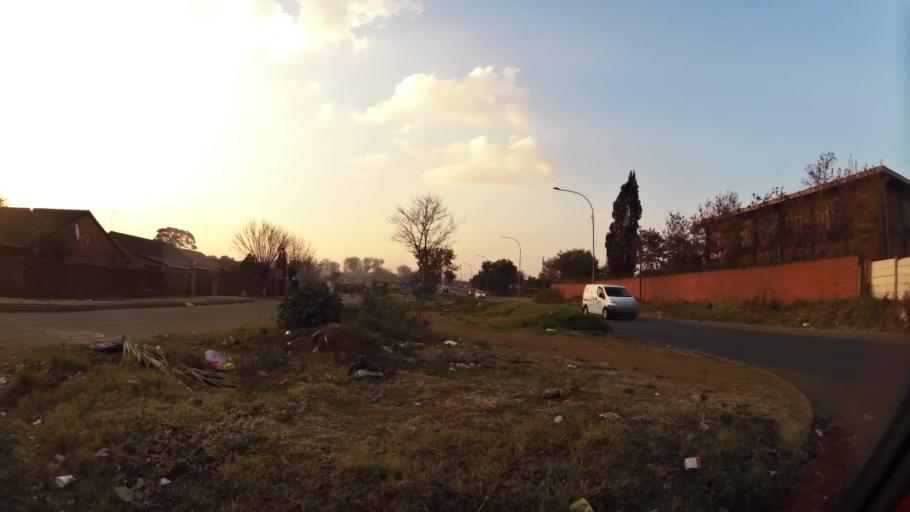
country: ZA
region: Gauteng
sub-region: City of Johannesburg Metropolitan Municipality
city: Soweto
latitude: -26.2875
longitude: 27.8910
